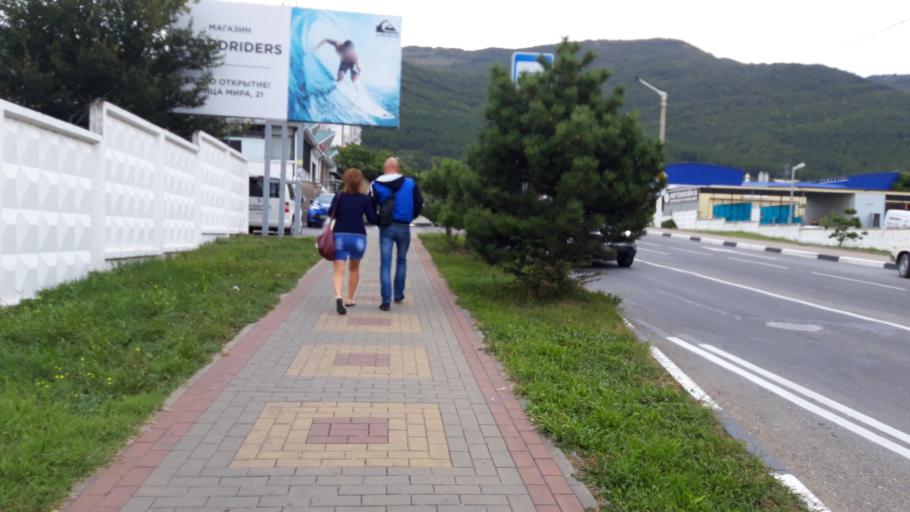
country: RU
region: Krasnodarskiy
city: Gelendzhik
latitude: 44.5694
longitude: 38.0909
